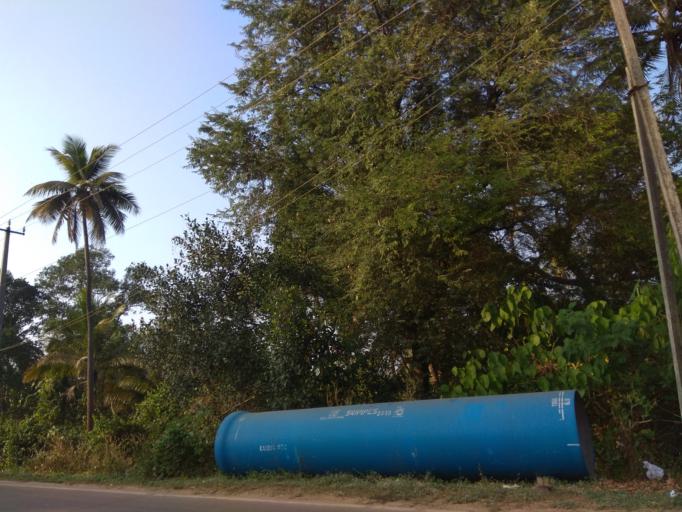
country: IN
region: Karnataka
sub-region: Dakshina Kannada
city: Mangalore
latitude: 12.9105
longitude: 74.8529
